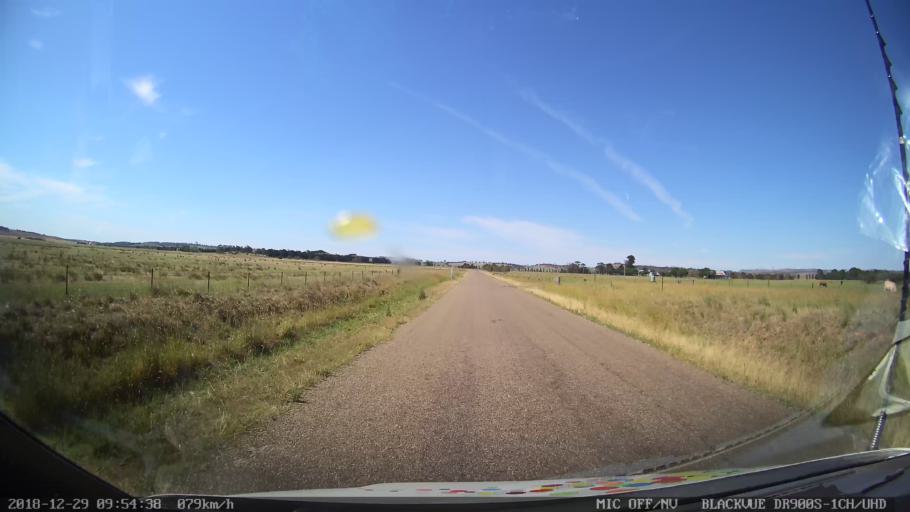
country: AU
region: New South Wales
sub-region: Goulburn Mulwaree
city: Goulburn
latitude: -34.7657
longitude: 149.4665
